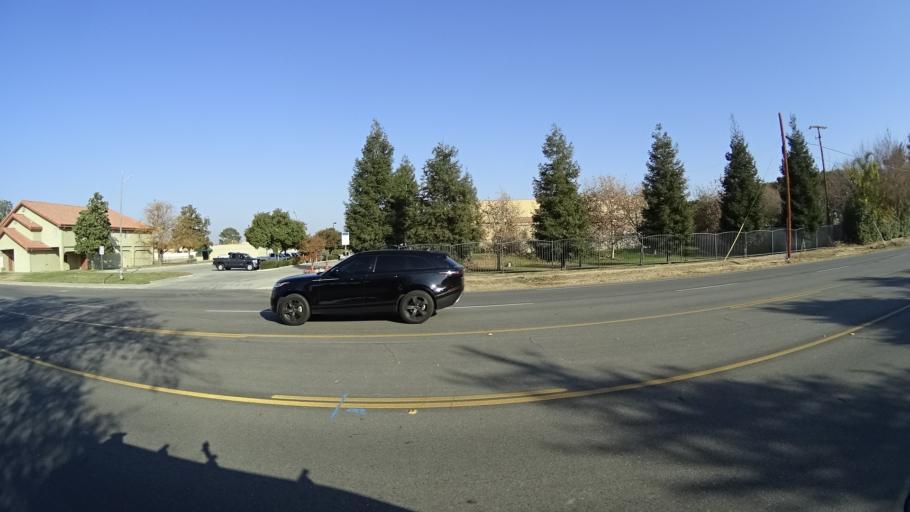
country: US
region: California
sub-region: Kern County
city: Greenacres
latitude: 35.3689
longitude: -119.1211
